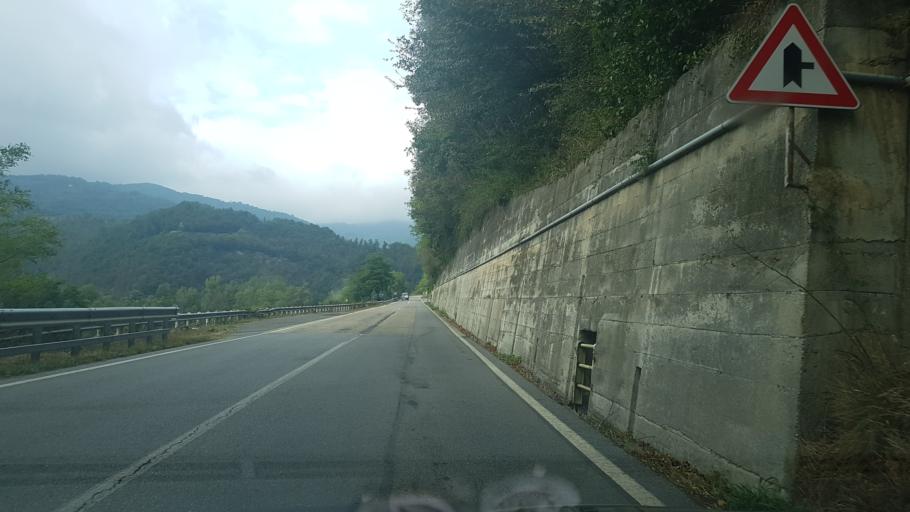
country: IT
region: Piedmont
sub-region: Provincia di Cuneo
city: Monesiglio
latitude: 44.4757
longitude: 8.1159
